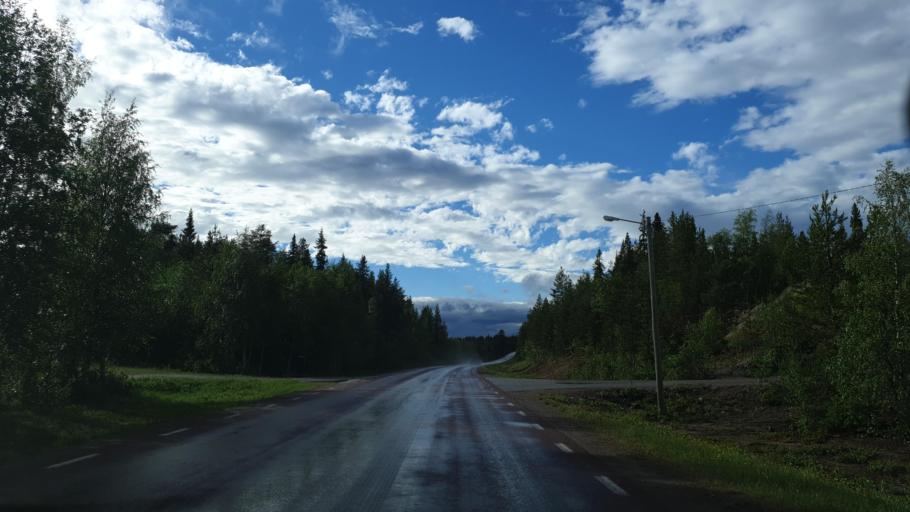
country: SE
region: Norrbotten
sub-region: Arjeplogs Kommun
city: Arjeplog
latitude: 66.0136
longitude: 18.0852
